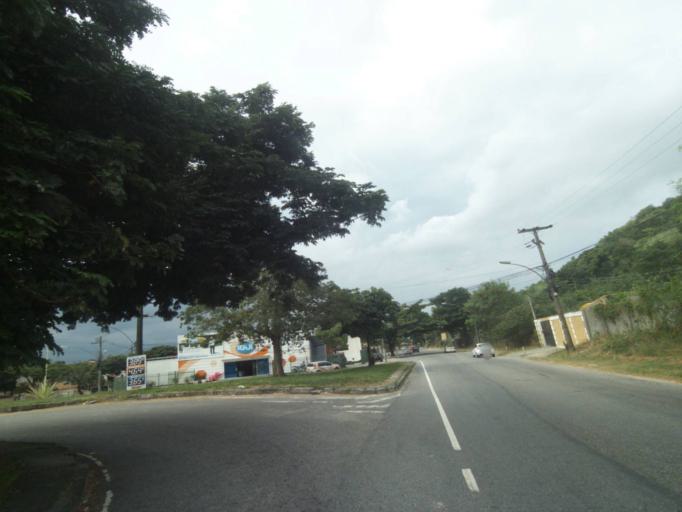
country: BR
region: Rio de Janeiro
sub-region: Nilopolis
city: Nilopolis
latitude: -22.8930
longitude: -43.3949
